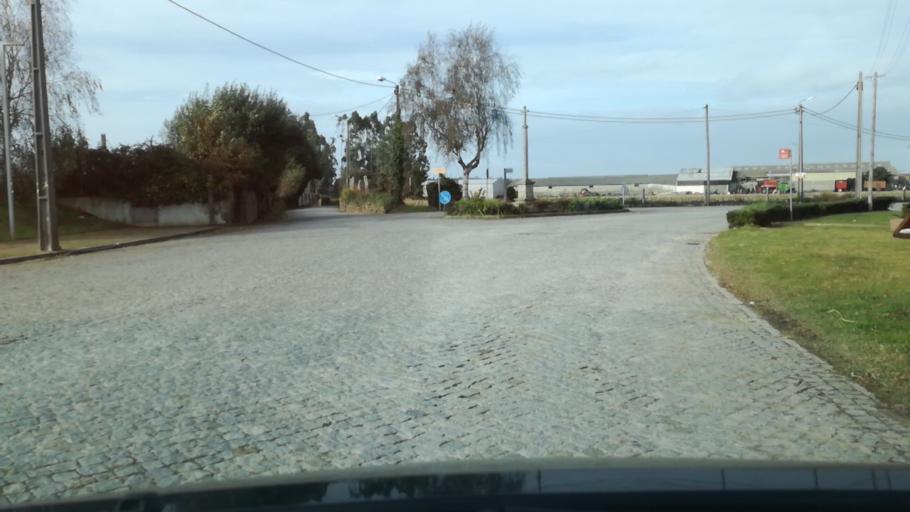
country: PT
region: Porto
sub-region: Matosinhos
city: Santa Cruz do Bispo
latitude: 41.2540
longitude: -8.6755
